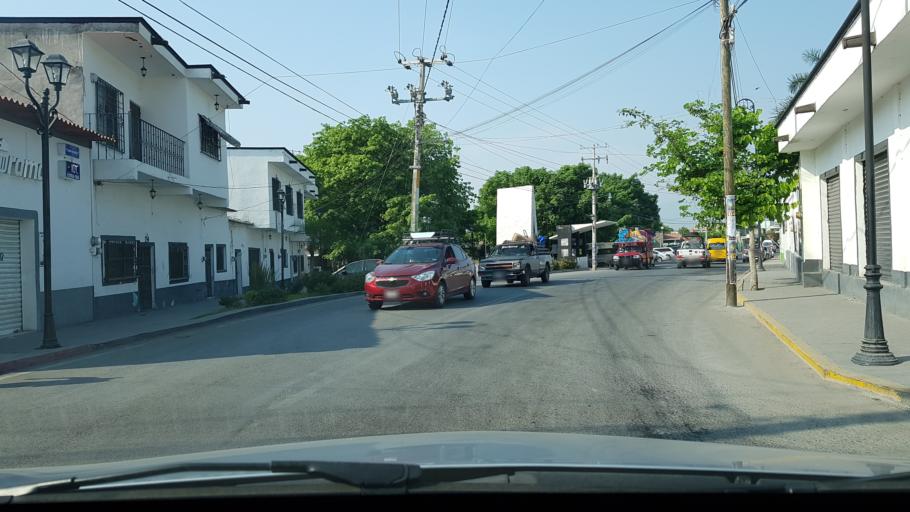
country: MX
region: Morelos
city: Tlaquiltenango
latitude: 18.6283
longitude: -99.1623
